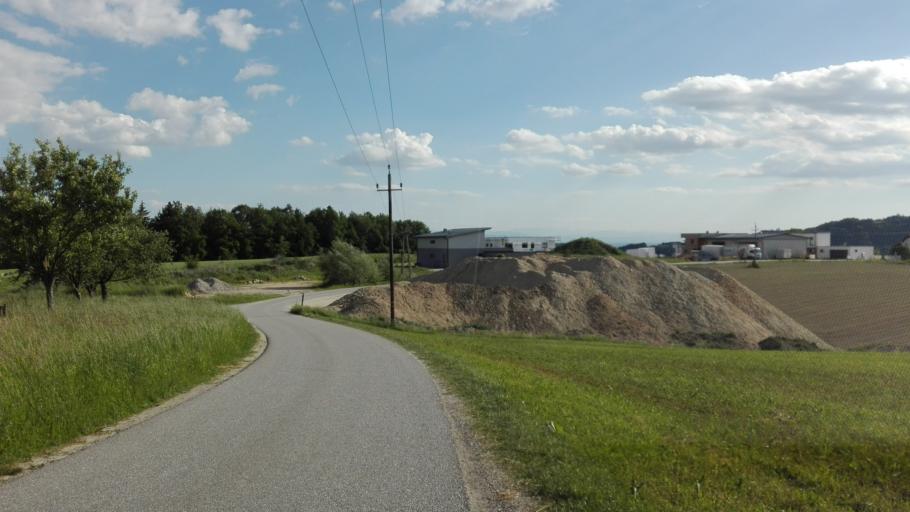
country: AT
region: Upper Austria
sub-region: Politischer Bezirk Perg
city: Perg
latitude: 48.3246
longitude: 14.6212
